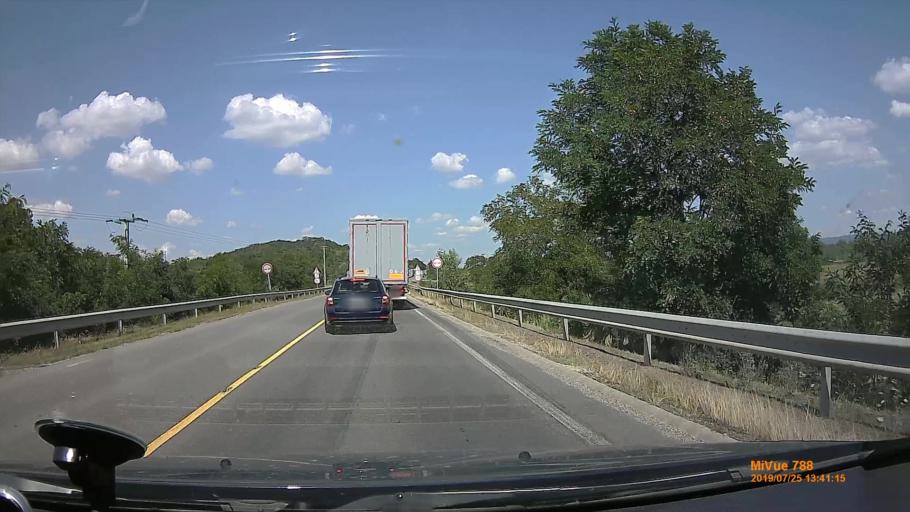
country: HU
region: Borsod-Abauj-Zemplen
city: Gonc
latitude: 48.4454
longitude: 21.1865
